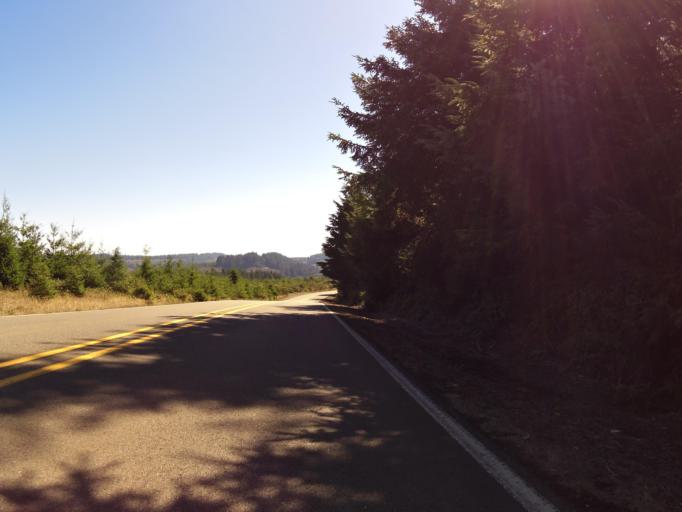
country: US
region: Oregon
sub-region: Coos County
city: Barview
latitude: 43.2467
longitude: -124.3338
